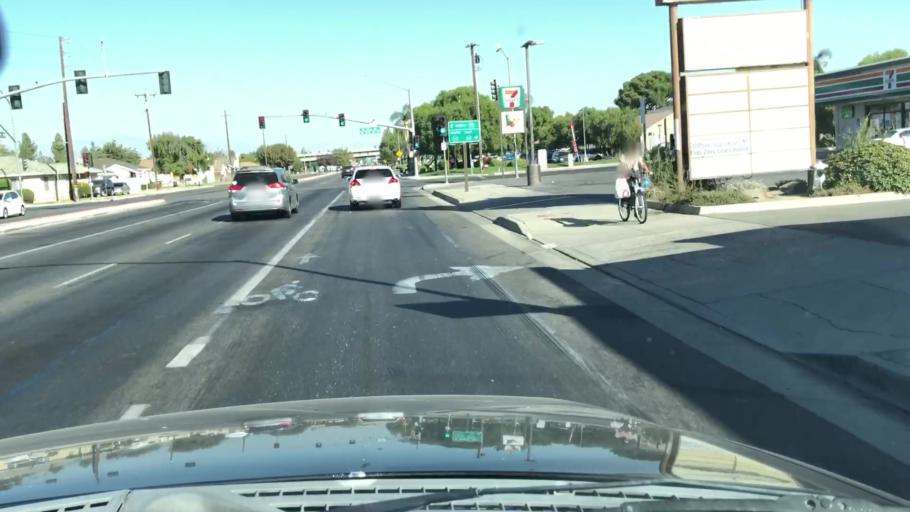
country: US
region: California
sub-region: Kern County
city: Bakersfield
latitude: 35.3541
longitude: -119.0442
